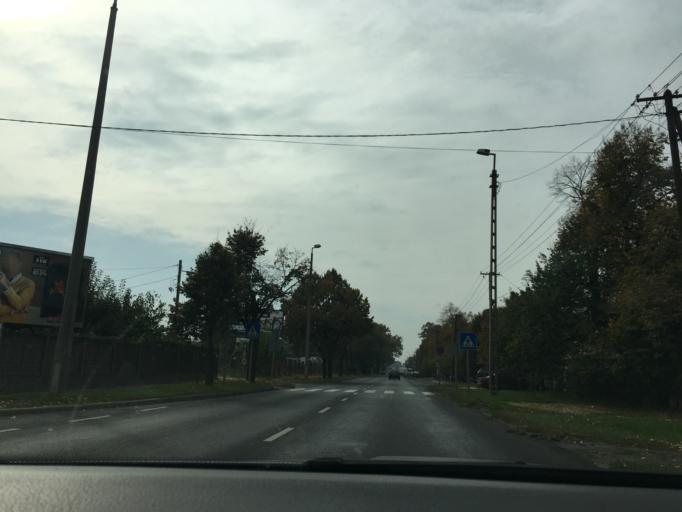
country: HU
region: Hajdu-Bihar
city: Debrecen
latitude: 47.5173
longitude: 21.6097
